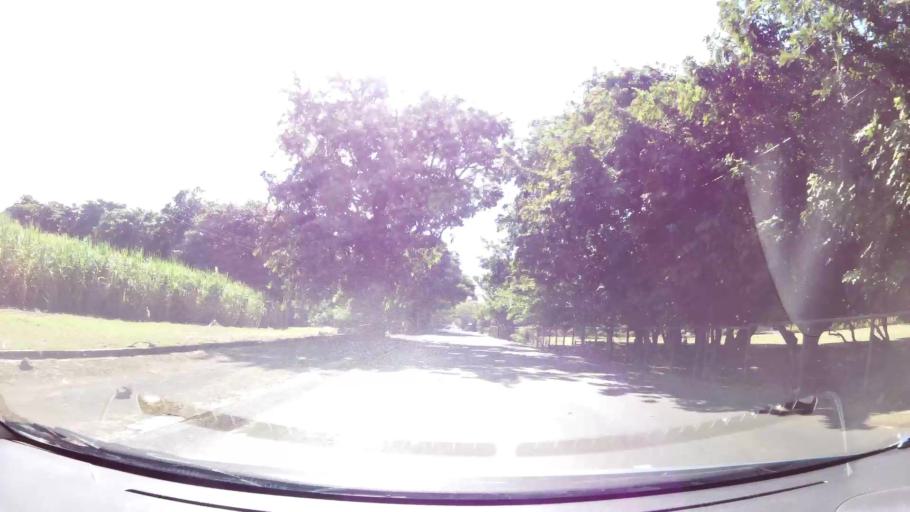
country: MU
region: Black River
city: Cascavelle
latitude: -20.2622
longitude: 57.4074
